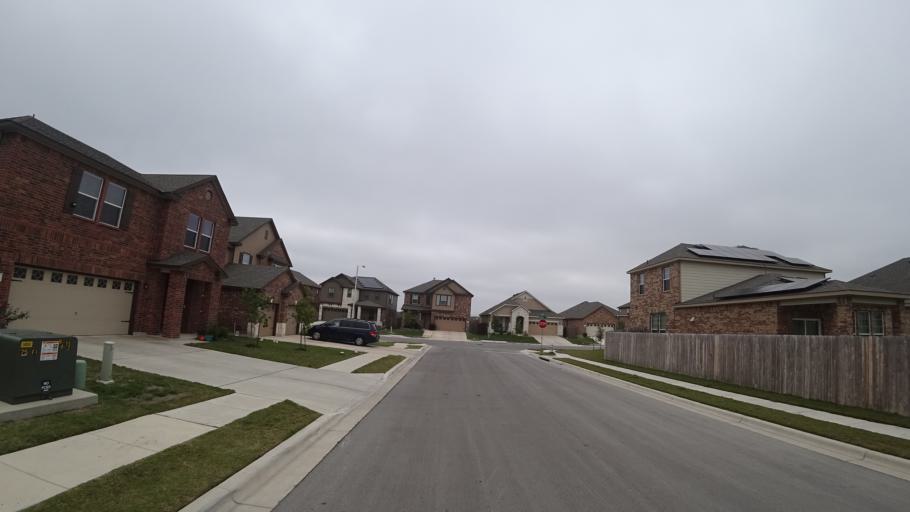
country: US
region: Texas
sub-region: Travis County
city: Pflugerville
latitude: 30.3929
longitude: -97.6496
